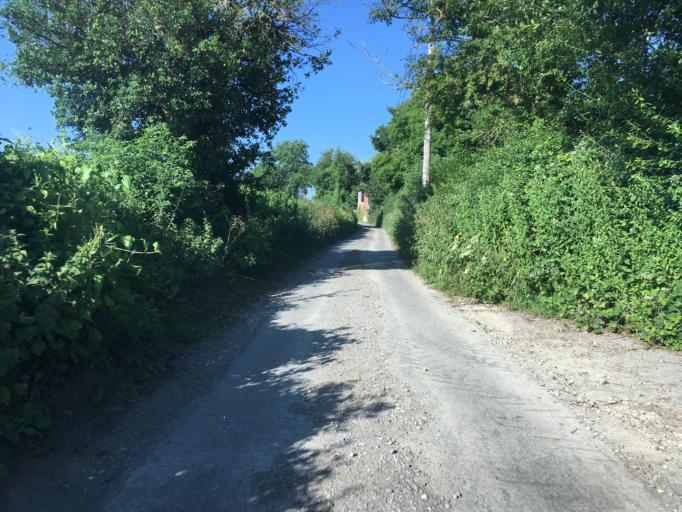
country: GB
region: England
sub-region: South Gloucestershire
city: Siston
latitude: 51.4647
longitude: -2.4400
